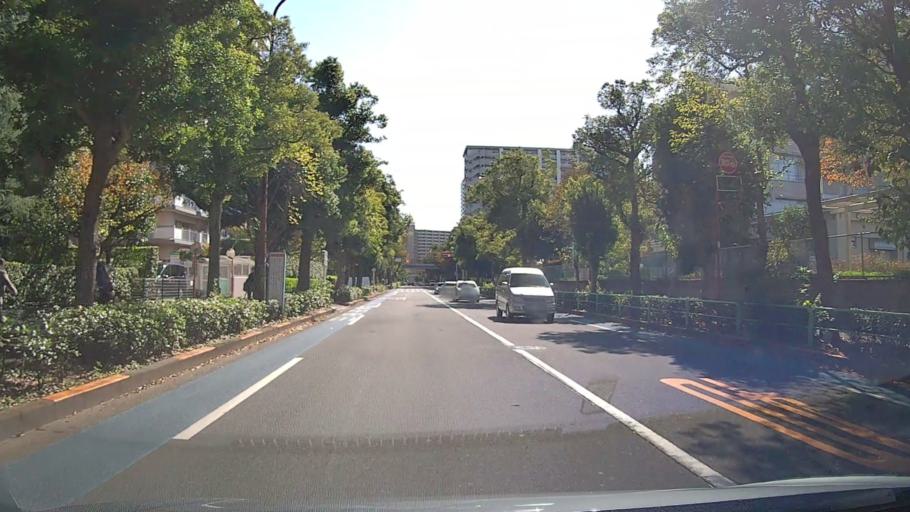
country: JP
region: Saitama
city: Wako
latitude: 35.7620
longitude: 139.6254
